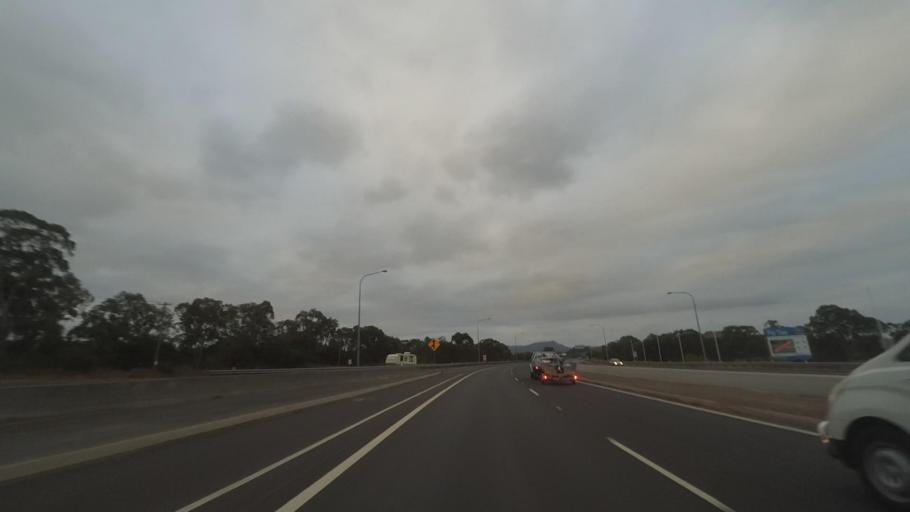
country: AU
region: New South Wales
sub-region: Shellharbour
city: Albion Park Rail
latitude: -34.5402
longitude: 150.7845
